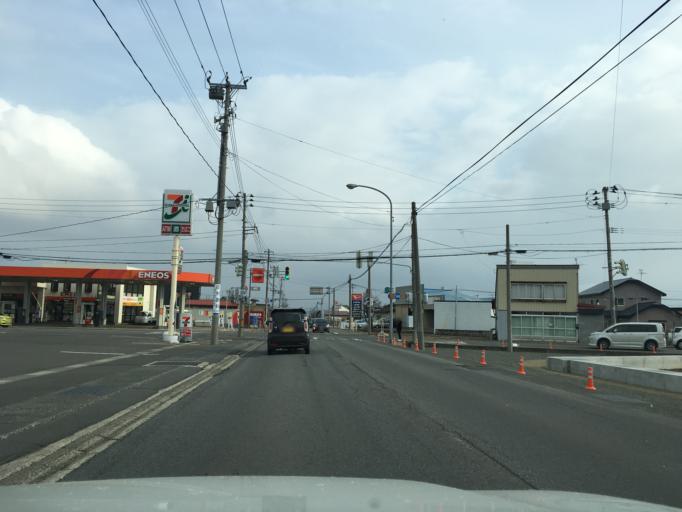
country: JP
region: Aomori
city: Namioka
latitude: 40.7091
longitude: 140.5904
